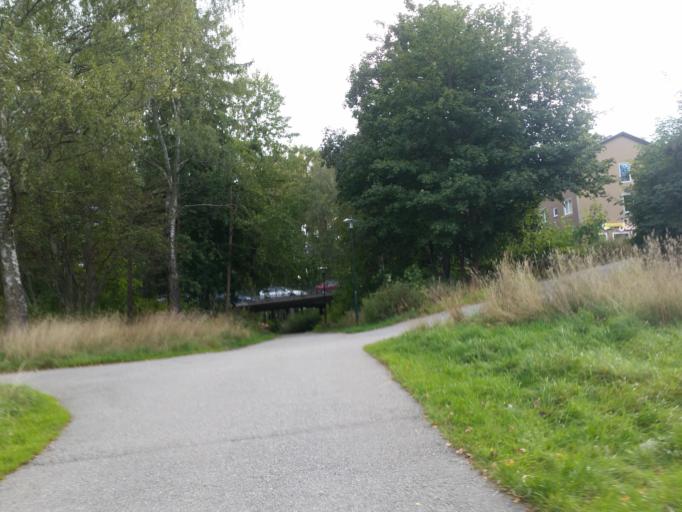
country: SE
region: Stockholm
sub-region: Stockholms Kommun
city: OEstermalm
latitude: 59.2879
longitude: 18.1090
